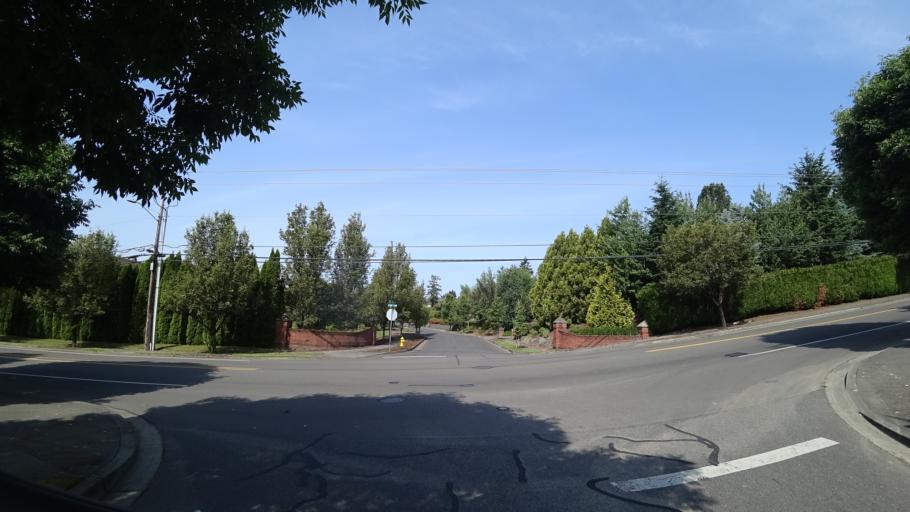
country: US
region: Oregon
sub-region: Clackamas County
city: Happy Valley
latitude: 45.4567
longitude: -122.5141
